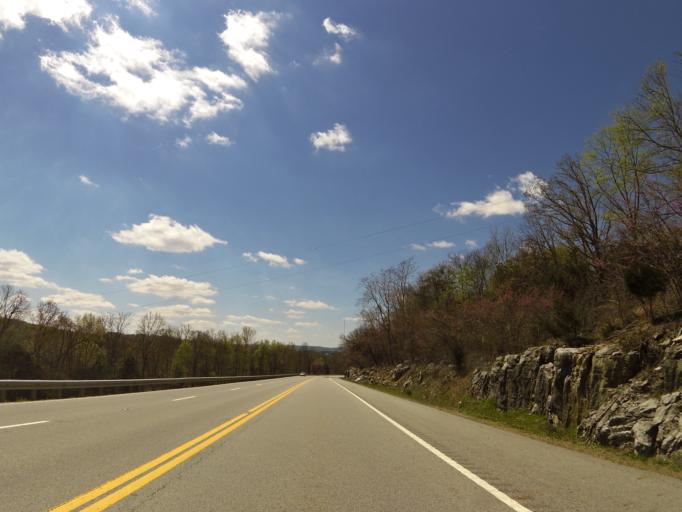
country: US
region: Tennessee
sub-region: White County
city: Sparta
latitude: 35.9256
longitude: -85.4399
